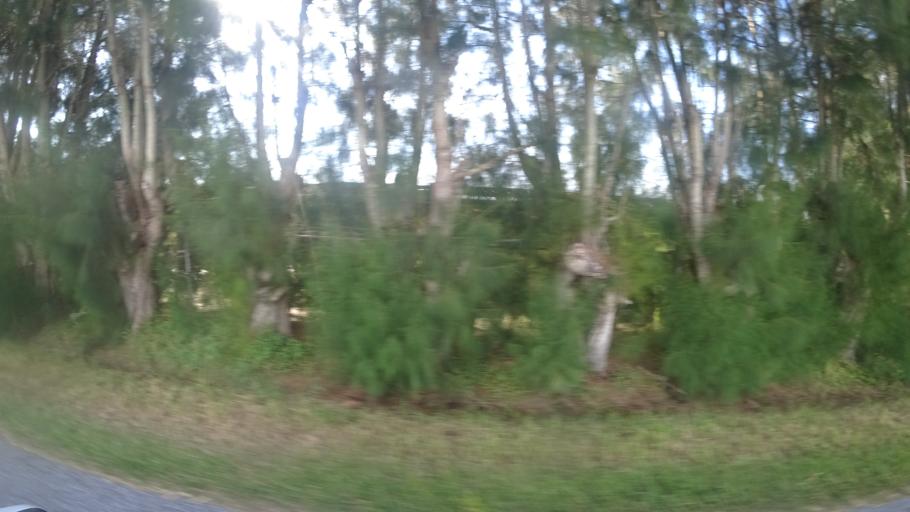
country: US
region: Florida
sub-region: Manatee County
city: West Bradenton
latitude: 27.5278
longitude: -82.6159
